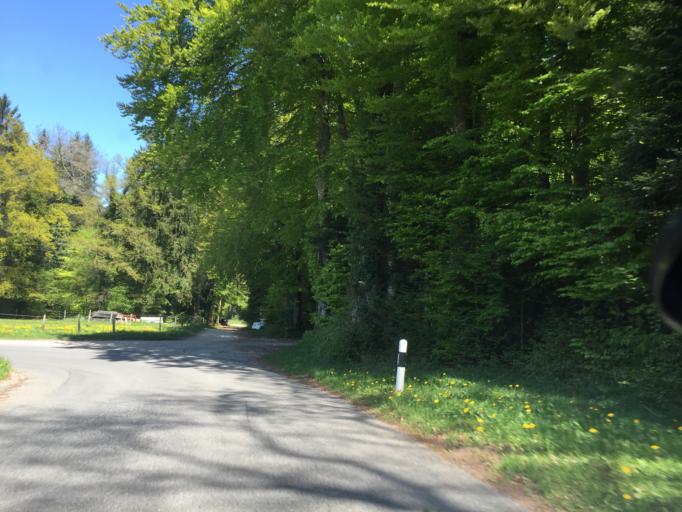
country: CH
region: Vaud
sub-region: Morges District
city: Mauraz
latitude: 46.6042
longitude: 6.4276
